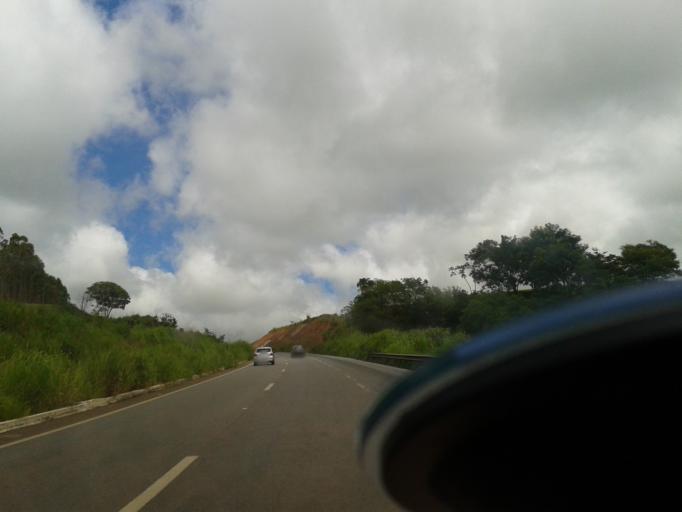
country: BR
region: Goias
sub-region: Itaberai
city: Itaberai
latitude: -16.1595
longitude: -49.6240
